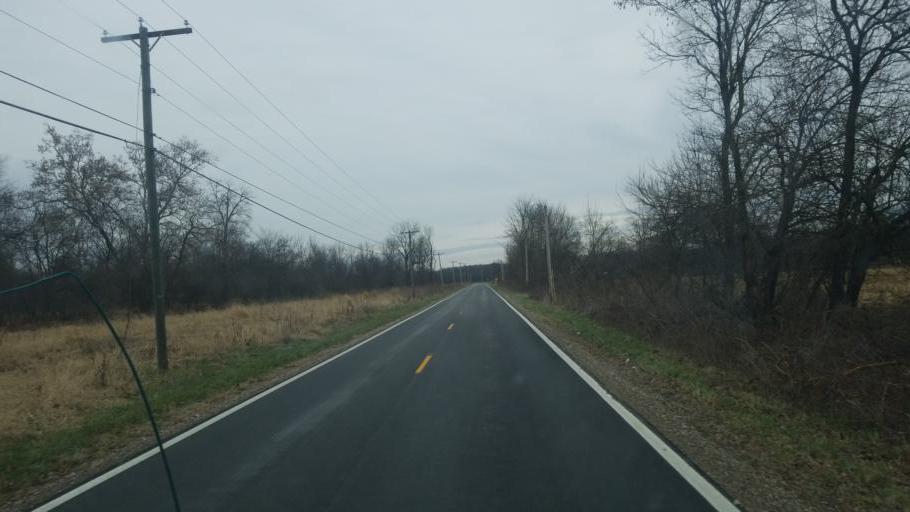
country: US
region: Ohio
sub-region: Licking County
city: Utica
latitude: 40.2525
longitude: -82.5149
